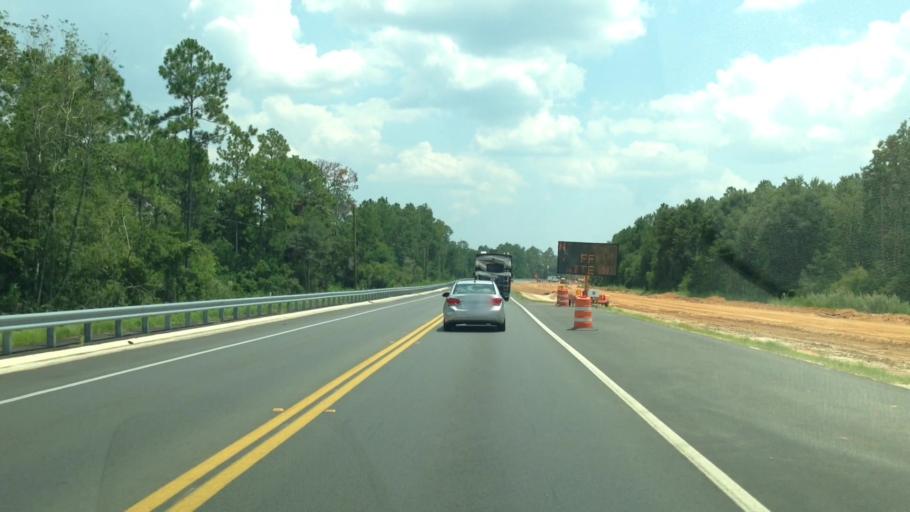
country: US
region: Florida
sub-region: Santa Rosa County
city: East Milton
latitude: 30.5865
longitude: -86.9326
